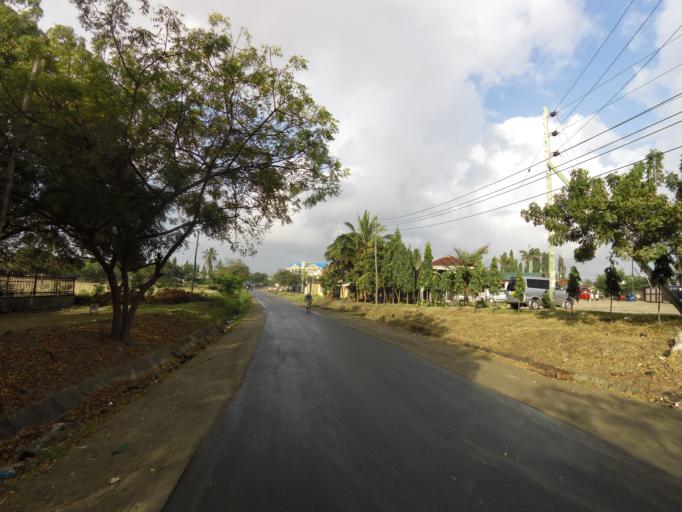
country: TZ
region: Dar es Salaam
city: Magomeni
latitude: -6.7842
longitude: 39.2370
